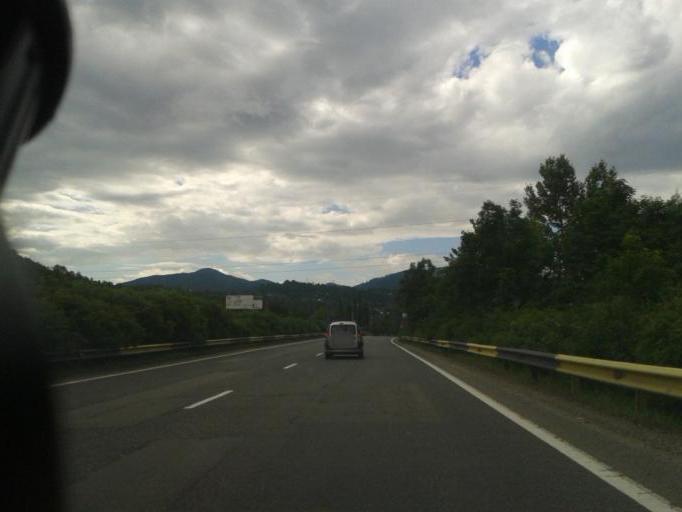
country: RO
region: Prahova
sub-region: Oras Breaza
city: Gura Beliei
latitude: 45.2222
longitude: 25.6436
